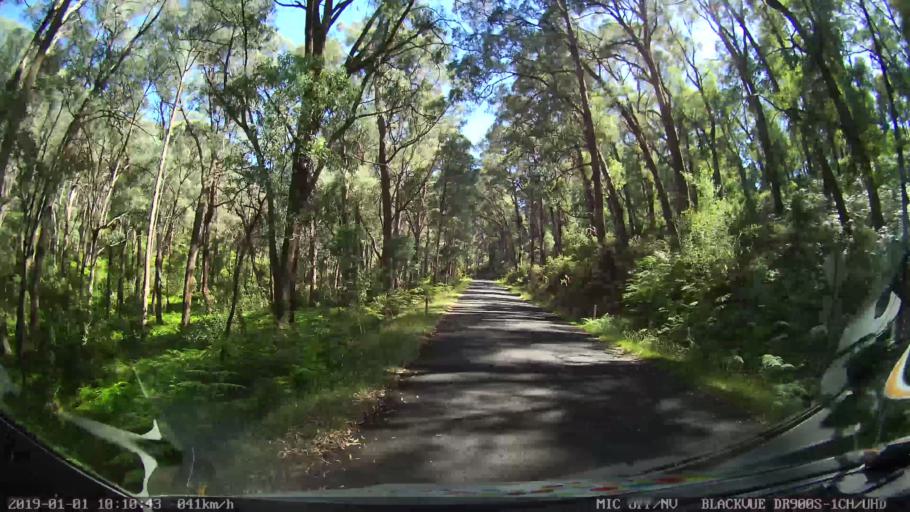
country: AU
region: New South Wales
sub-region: Snowy River
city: Jindabyne
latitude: -36.1394
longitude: 148.1580
